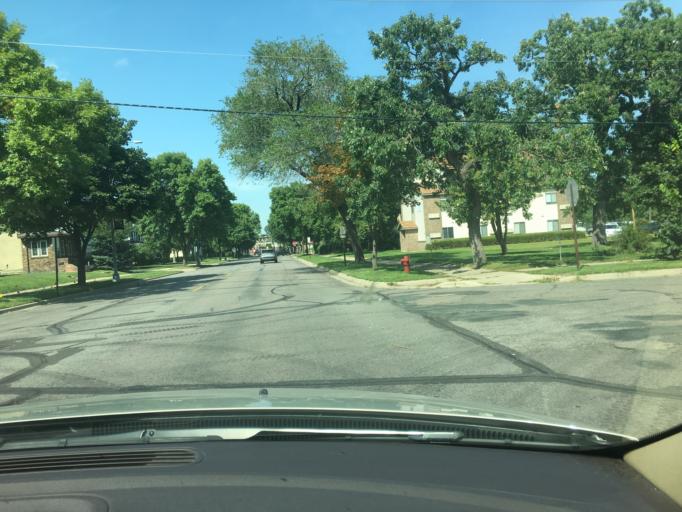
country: US
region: Minnesota
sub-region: Stearns County
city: Saint Cloud
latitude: 45.5548
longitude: -94.1546
